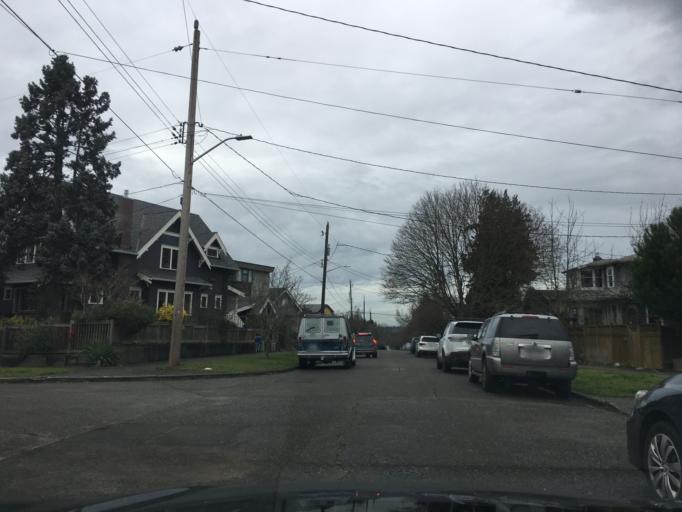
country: US
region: Washington
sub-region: King County
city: Seattle
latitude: 47.6664
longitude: -122.3315
